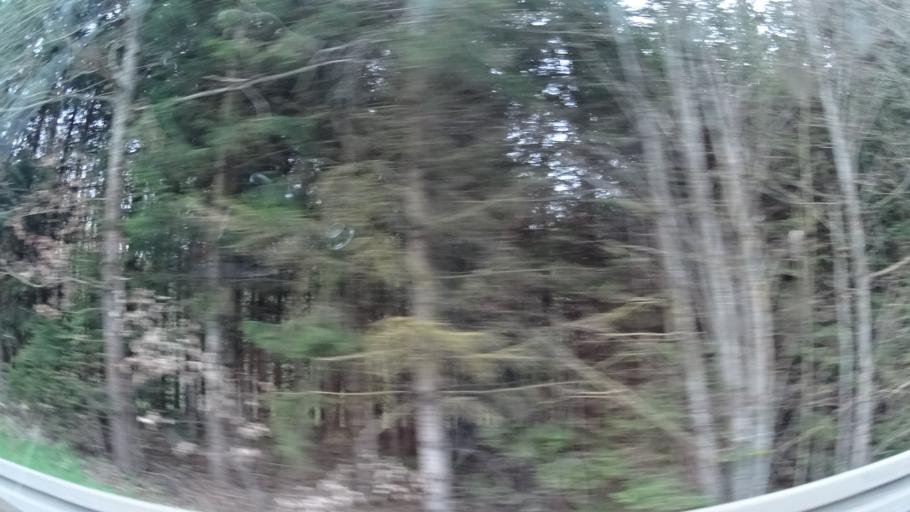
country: DE
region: Baden-Wuerttemberg
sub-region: Freiburg Region
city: Niedereschach
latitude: 48.1156
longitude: 8.5131
